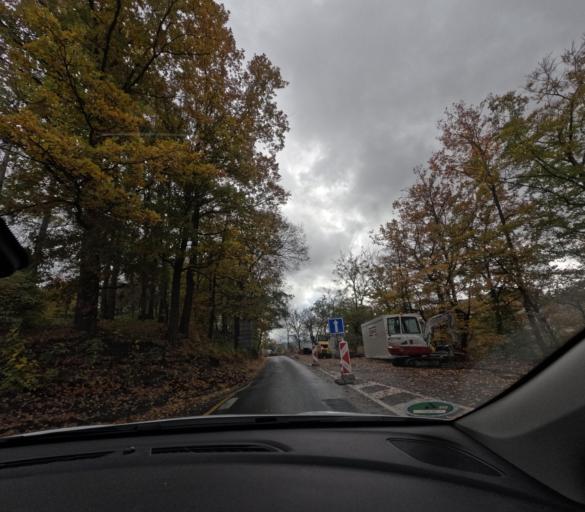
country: CZ
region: Karlovarsky
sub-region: Okres Karlovy Vary
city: Karlovy Vary
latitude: 50.2303
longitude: 12.8770
